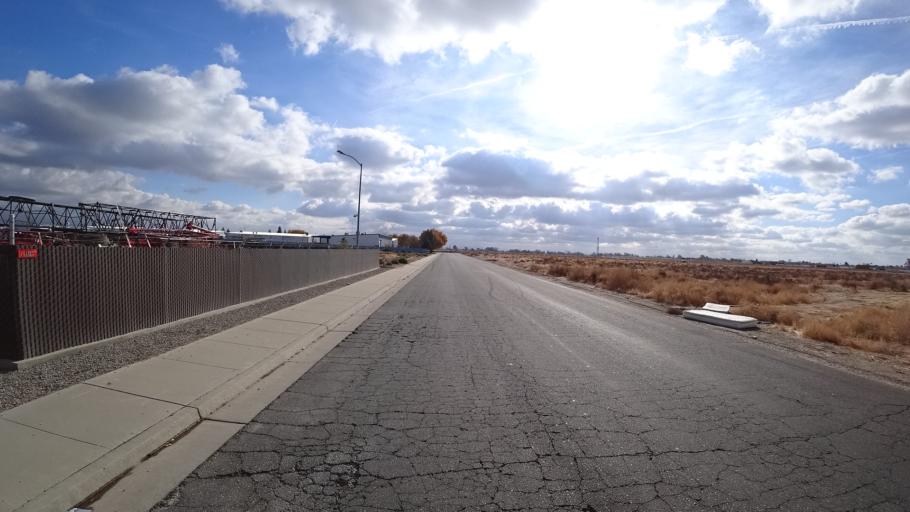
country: US
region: California
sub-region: Kern County
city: Bakersfield
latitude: 35.3487
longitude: -118.9764
